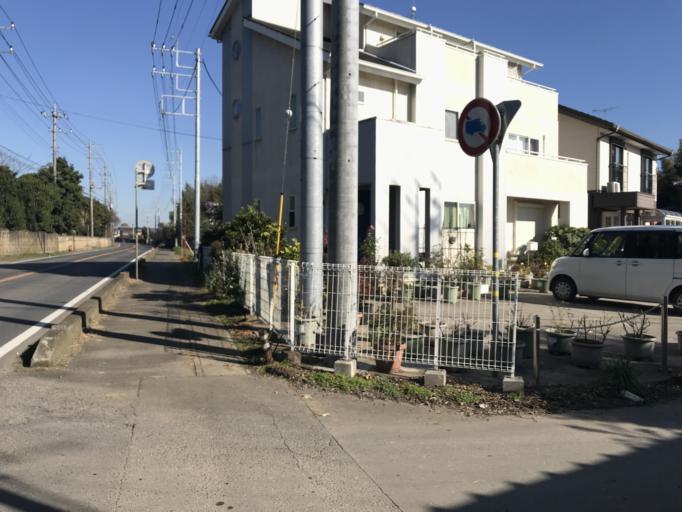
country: JP
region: Ibaraki
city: Yuki
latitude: 36.2691
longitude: 139.8449
